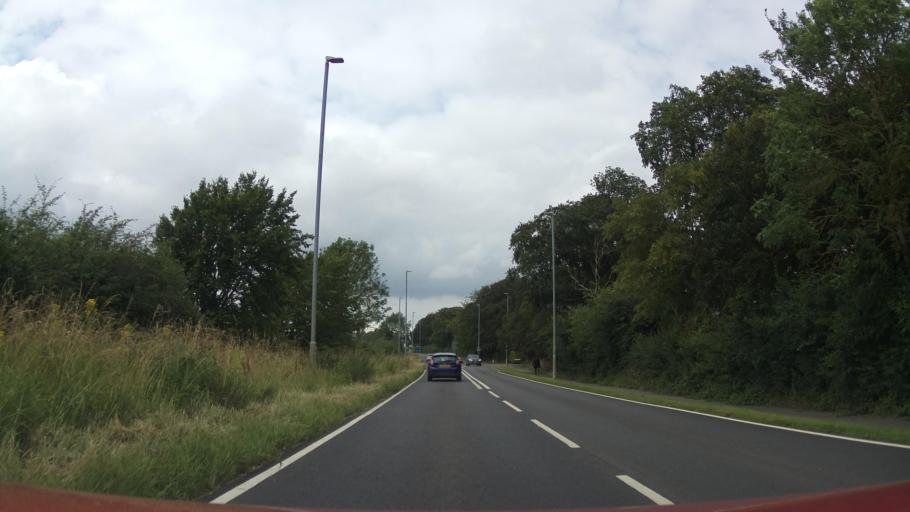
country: GB
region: England
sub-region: District of Rutland
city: Ryhall
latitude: 52.6797
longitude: -0.4725
